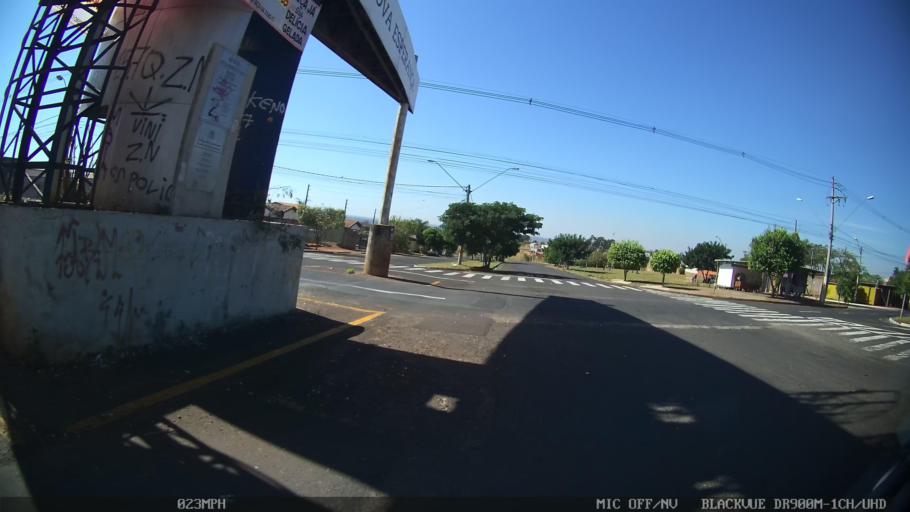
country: BR
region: Sao Paulo
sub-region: Sao Jose Do Rio Preto
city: Sao Jose do Rio Preto
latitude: -20.7468
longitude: -49.4080
